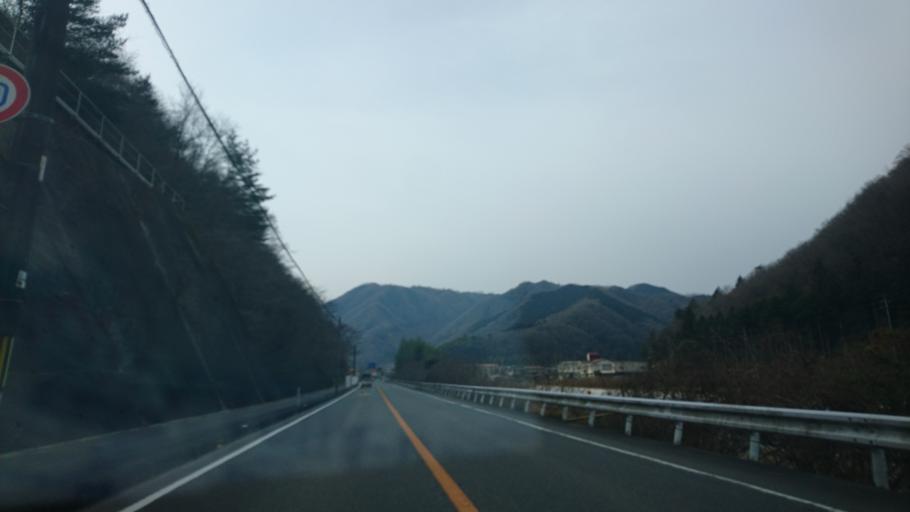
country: JP
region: Okayama
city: Takahashi
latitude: 34.8265
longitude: 133.6228
